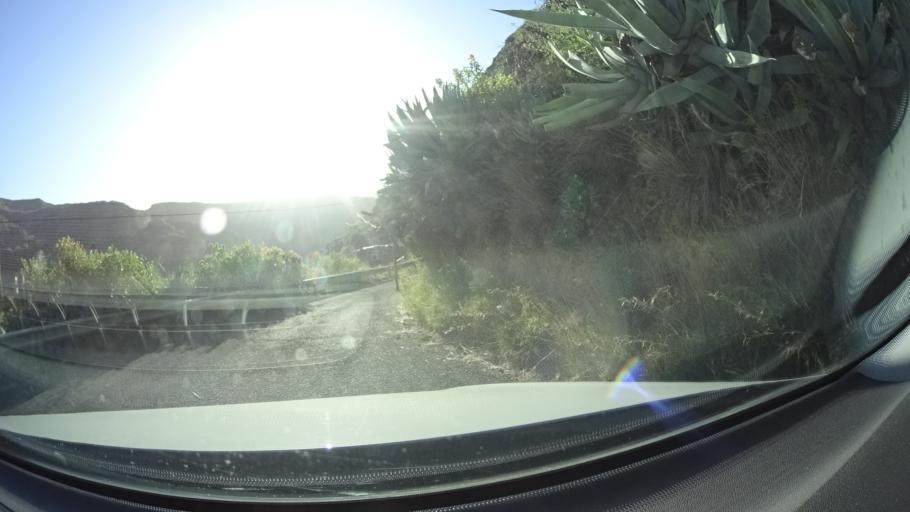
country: ES
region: Canary Islands
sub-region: Provincia de Las Palmas
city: Artenara
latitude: 28.0465
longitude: -15.6606
